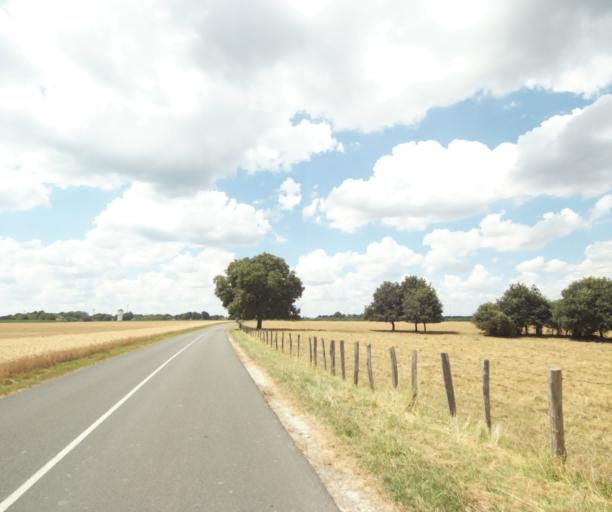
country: FR
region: Ile-de-France
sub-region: Departement de Seine-et-Marne
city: Hericy
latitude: 48.4424
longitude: 2.7894
